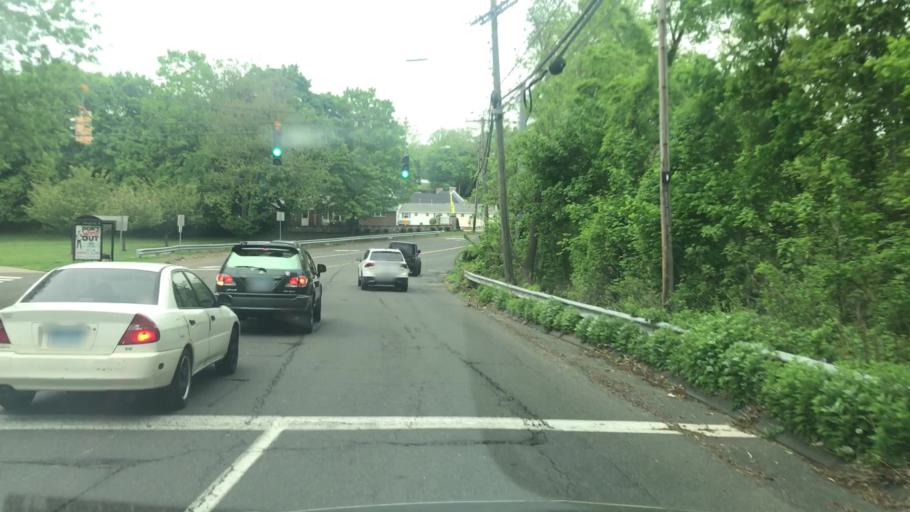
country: US
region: Connecticut
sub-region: Fairfield County
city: Stamford
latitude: 41.0571
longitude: -73.5587
